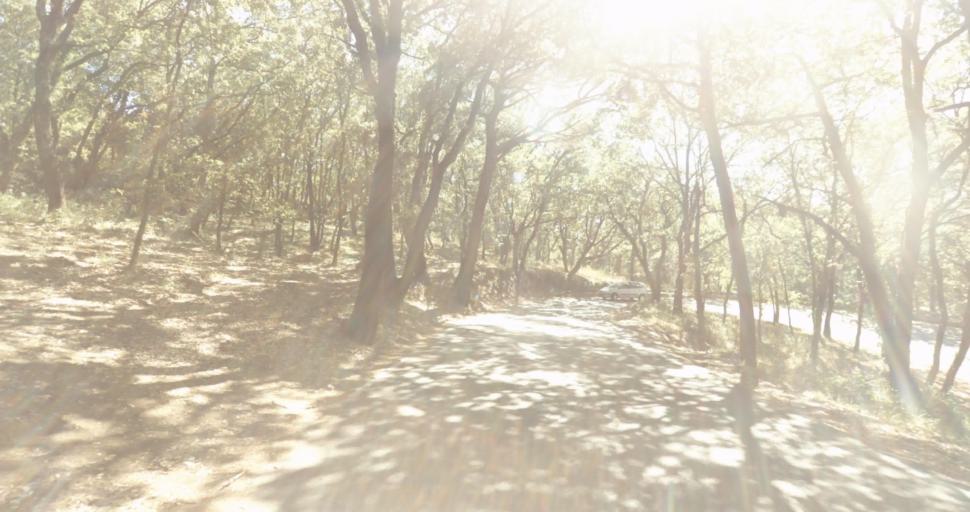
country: FR
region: Provence-Alpes-Cote d'Azur
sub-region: Departement du Var
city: Gassin
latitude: 43.2297
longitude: 6.5837
